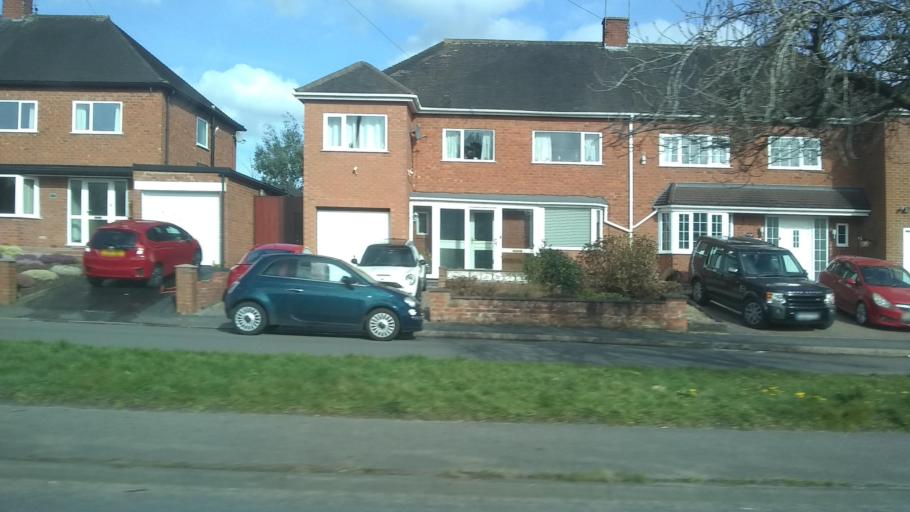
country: GB
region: England
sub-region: Worcestershire
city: Stourport-on-Severn
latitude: 52.3454
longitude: -2.2808
